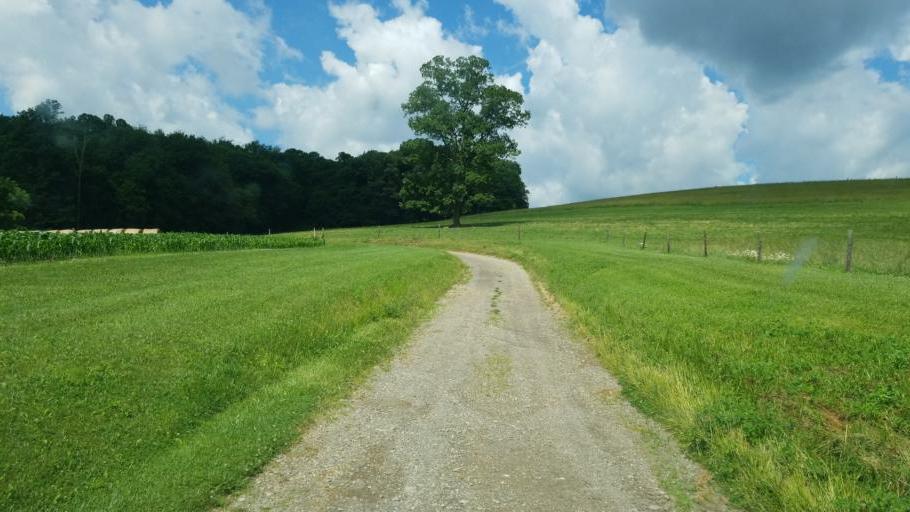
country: US
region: Ohio
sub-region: Knox County
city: Danville
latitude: 40.5181
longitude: -82.2549
